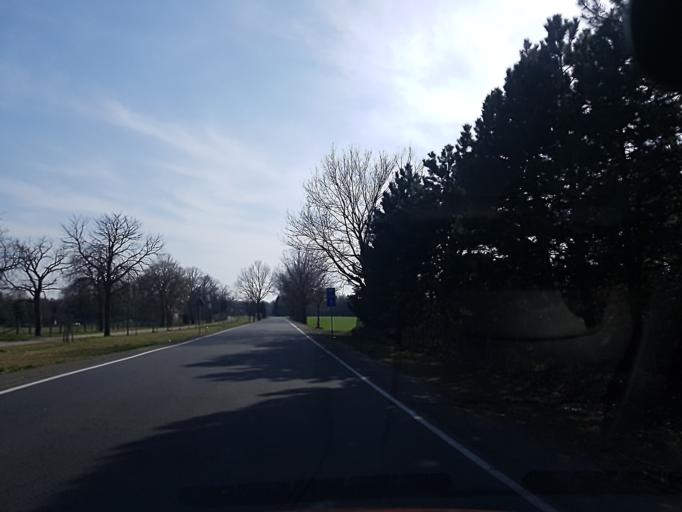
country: DE
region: Brandenburg
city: Bronkow
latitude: 51.6727
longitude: 13.9137
